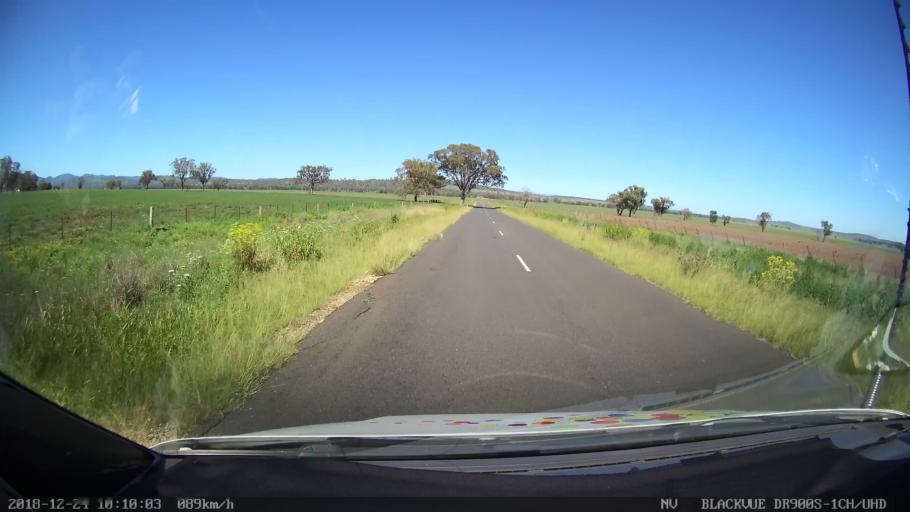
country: AU
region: New South Wales
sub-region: Liverpool Plains
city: Quirindi
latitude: -31.6662
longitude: 150.6815
